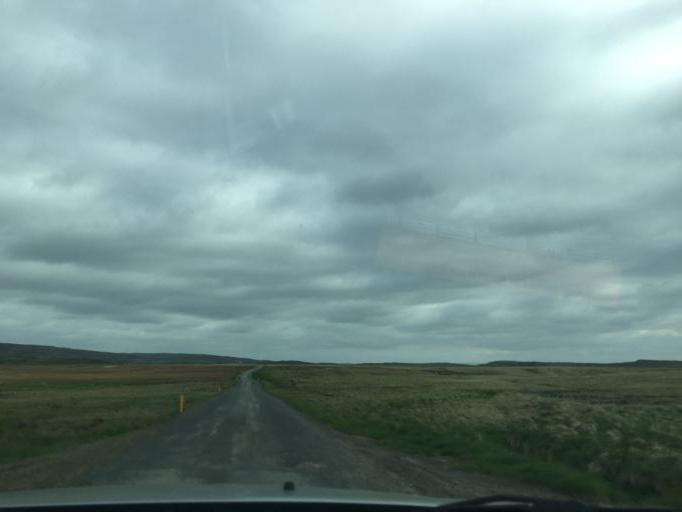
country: IS
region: South
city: Vestmannaeyjar
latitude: 64.2806
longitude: -20.2248
